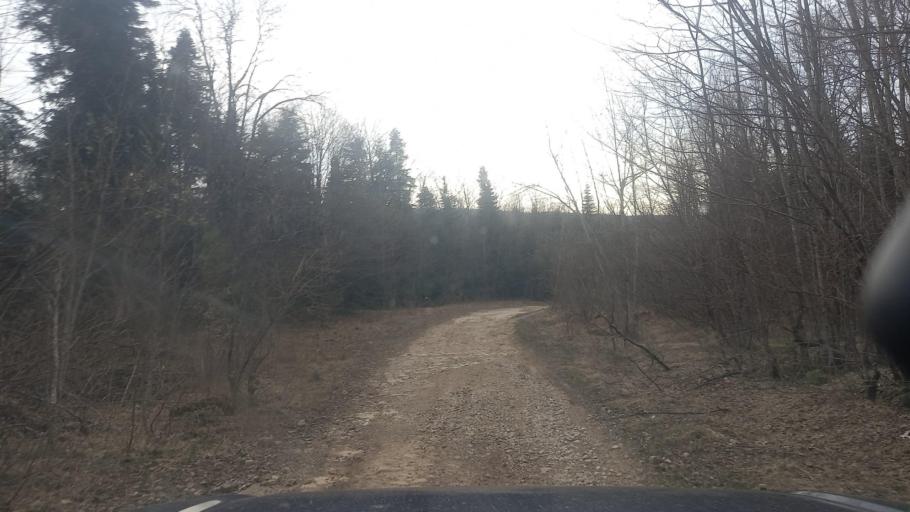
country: RU
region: Adygeya
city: Kamennomostskiy
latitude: 44.1863
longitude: 39.9823
